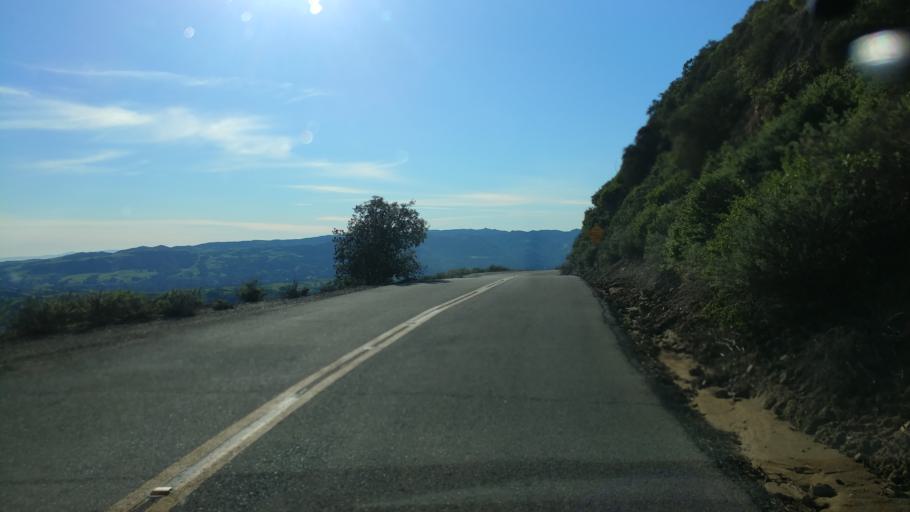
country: US
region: California
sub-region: Contra Costa County
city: Blackhawk
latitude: 37.8407
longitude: -121.9221
